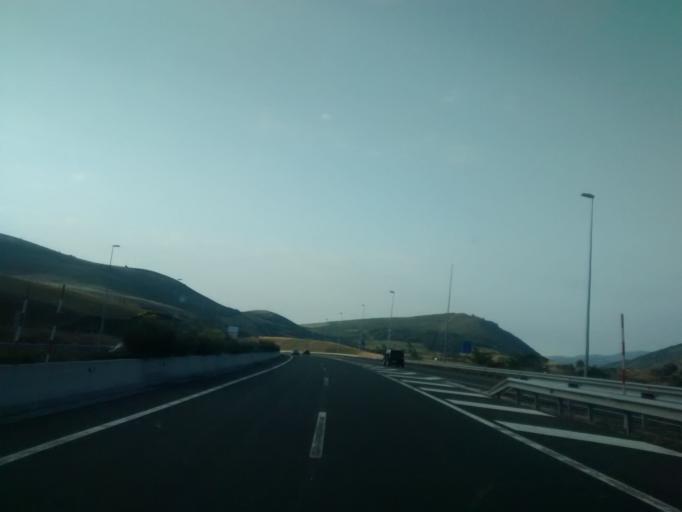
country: ES
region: Cantabria
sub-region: Provincia de Cantabria
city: Santiurde de Reinosa
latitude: 43.0701
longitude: -4.0861
